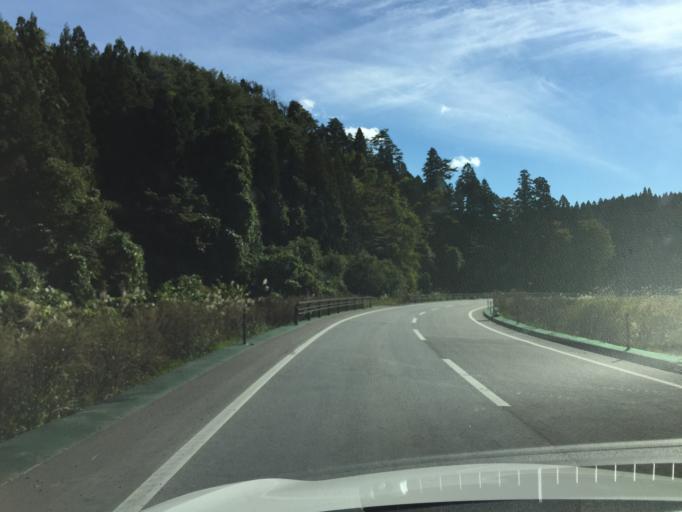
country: JP
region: Fukushima
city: Ishikawa
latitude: 37.1391
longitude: 140.5984
